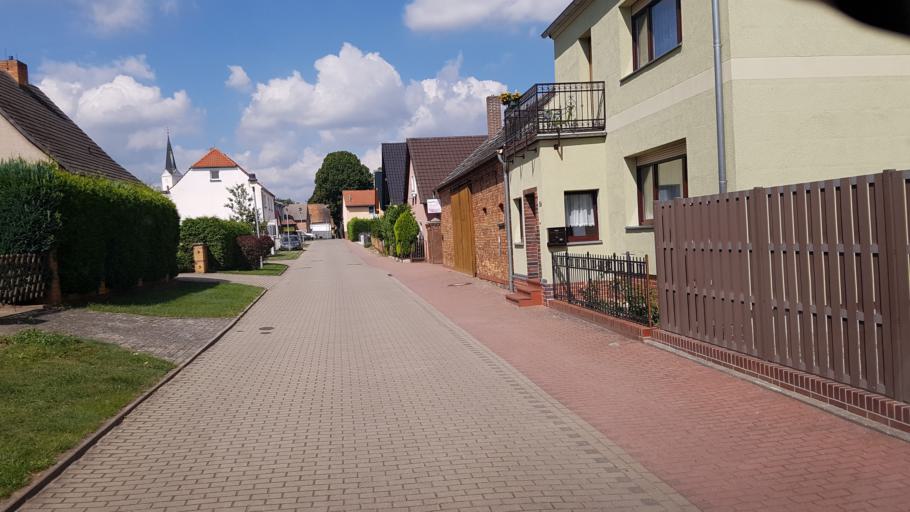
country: DE
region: Brandenburg
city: Lubbenau
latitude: 51.8608
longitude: 13.9327
